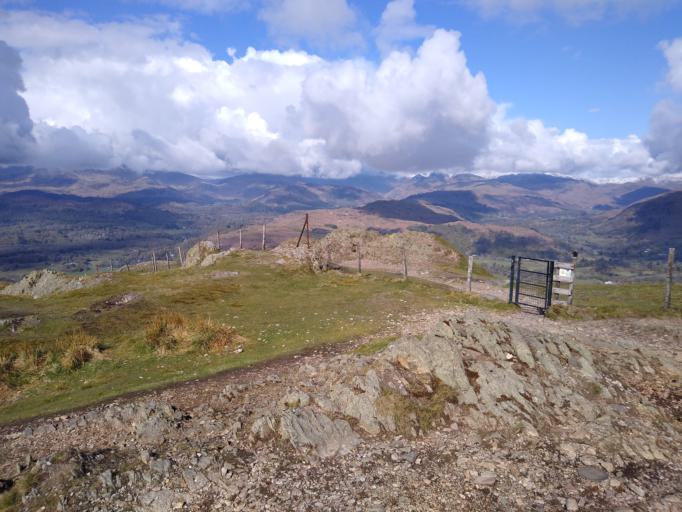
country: GB
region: England
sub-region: Cumbria
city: Ambleside
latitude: 54.4293
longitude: -2.9354
